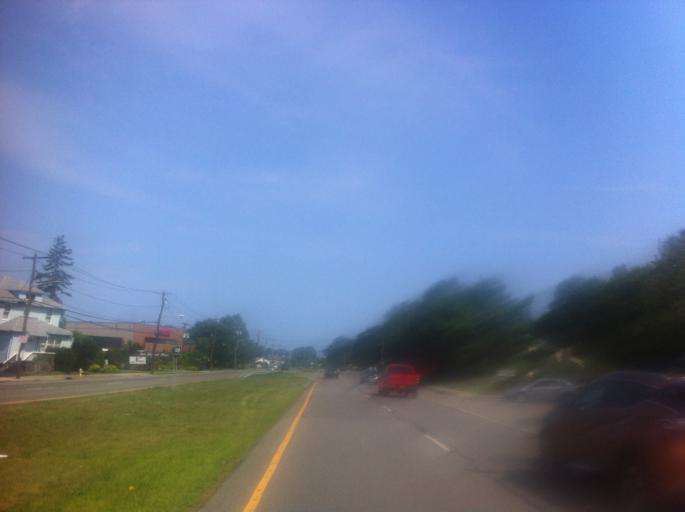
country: US
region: New York
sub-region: Suffolk County
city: West Babylon
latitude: 40.7082
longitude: -73.3539
